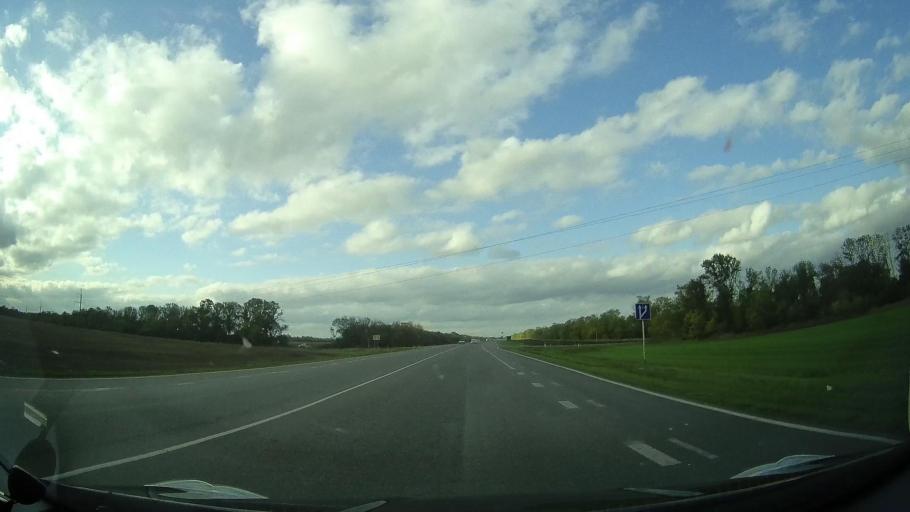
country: RU
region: Rostov
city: Kagal'nitskaya
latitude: 46.9286
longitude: 40.0979
